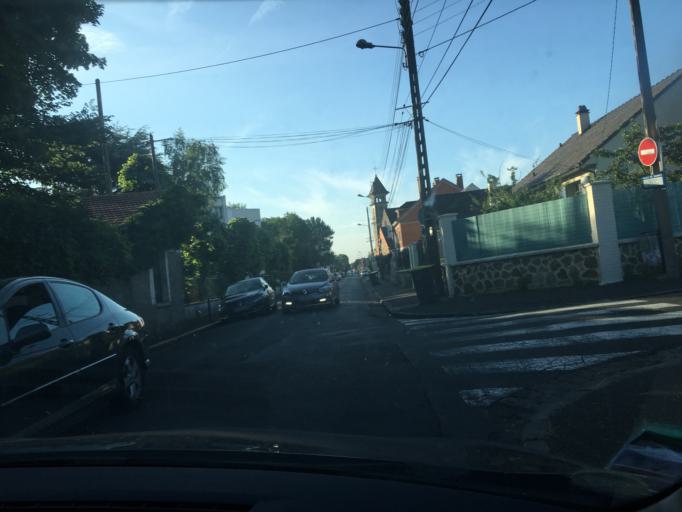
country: FR
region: Ile-de-France
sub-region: Departement de l'Essonne
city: Brunoy
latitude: 48.6938
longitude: 2.4908
